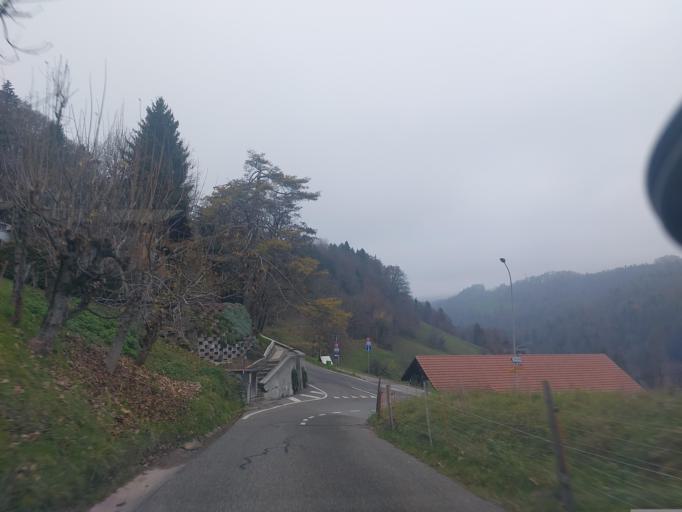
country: CH
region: Fribourg
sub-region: Veveyse District
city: Attalens
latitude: 46.4988
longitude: 6.8798
